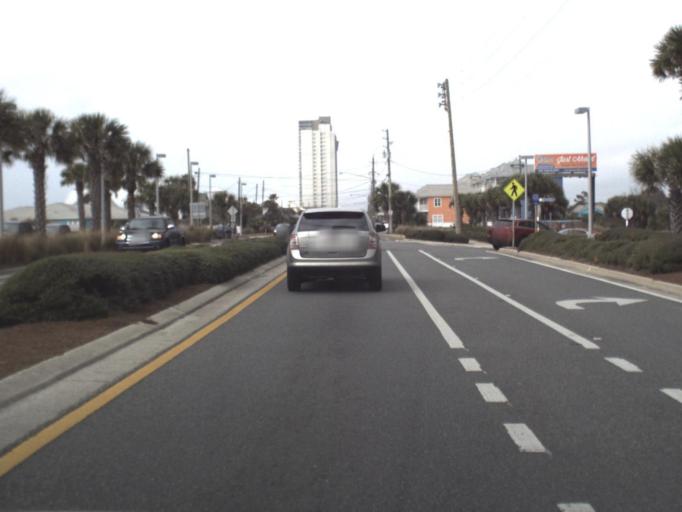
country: US
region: Florida
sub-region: Bay County
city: Laguna Beach
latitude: 30.2163
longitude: -85.8776
